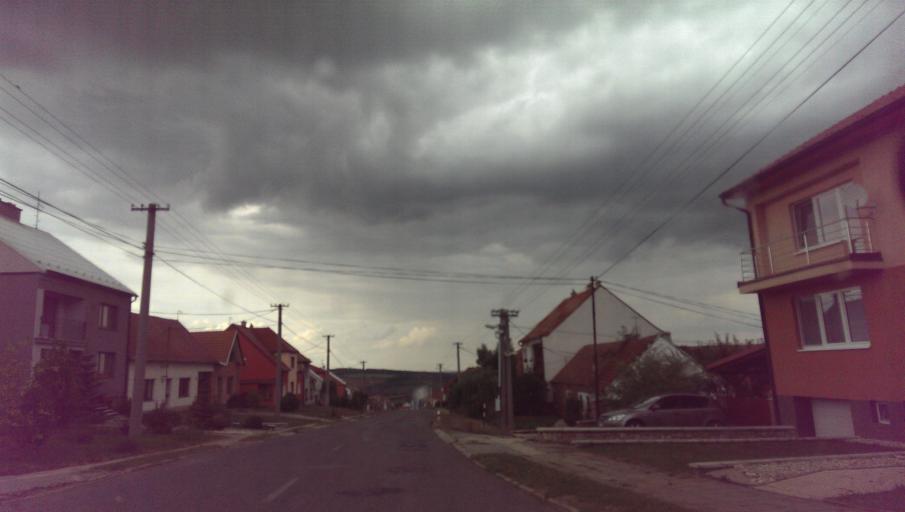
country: CZ
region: South Moravian
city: Velka nad Velickou
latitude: 48.9053
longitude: 17.5639
